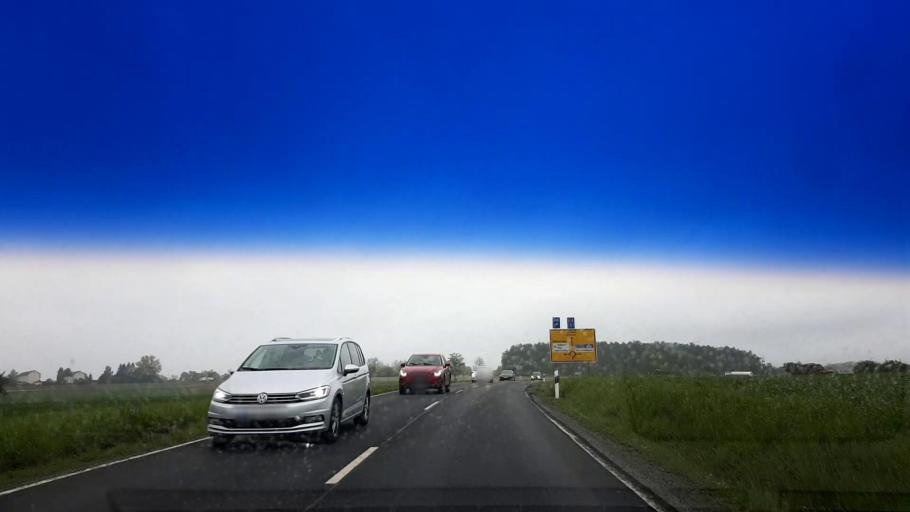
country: DE
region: Bavaria
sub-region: Upper Franconia
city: Bindlach
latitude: 50.0036
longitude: 11.6274
